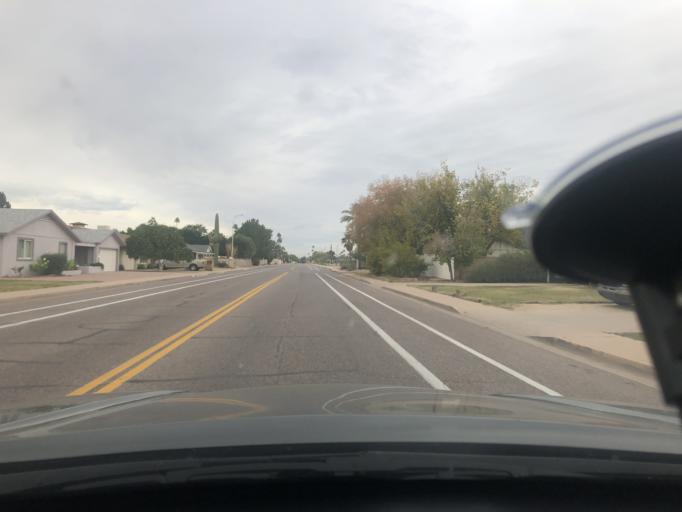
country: US
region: Arizona
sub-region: Maricopa County
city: Scottsdale
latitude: 33.4877
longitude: -111.8968
